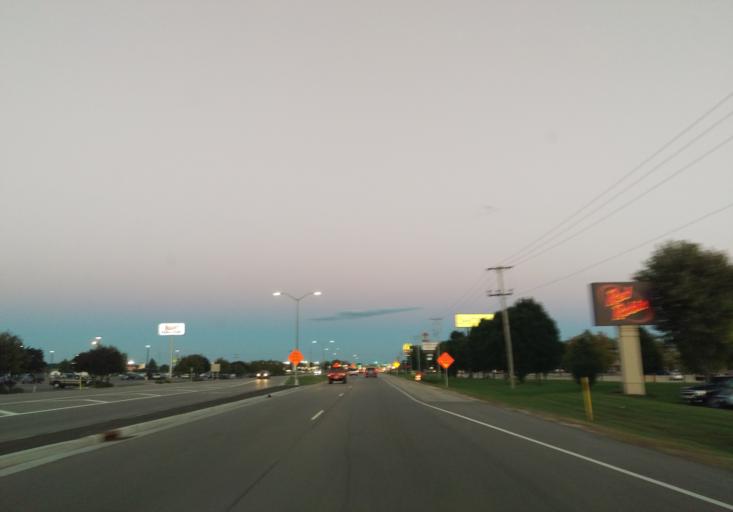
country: US
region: Wisconsin
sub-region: Rock County
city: Janesville
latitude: 42.7192
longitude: -88.9934
